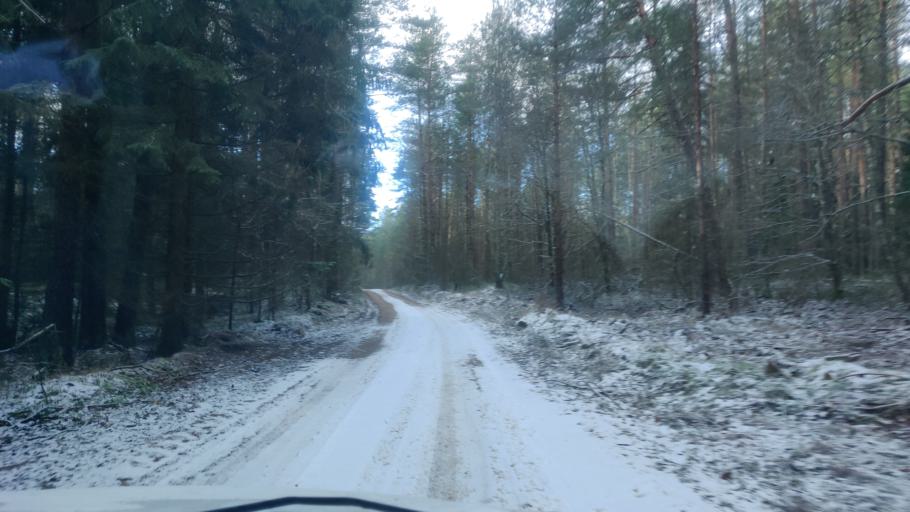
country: LT
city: Trakai
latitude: 54.5671
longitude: 24.9218
